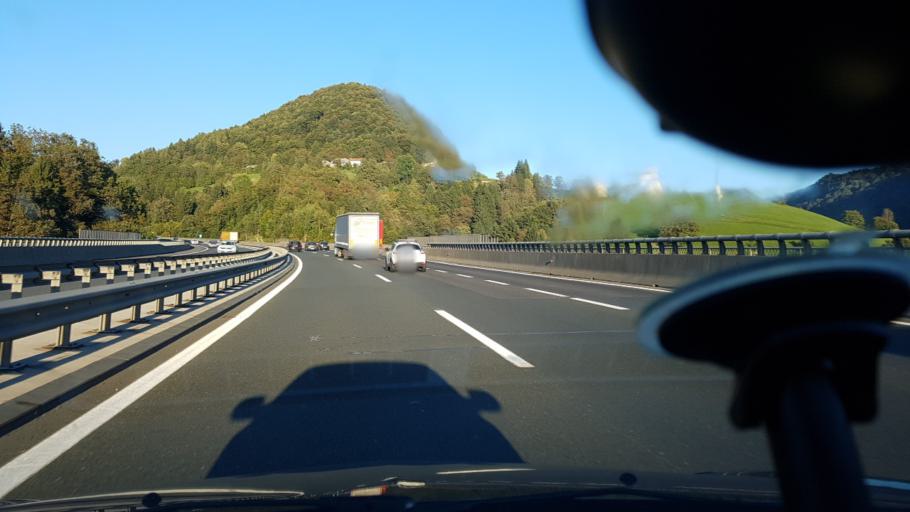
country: SI
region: Moravce
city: Moravce
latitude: 46.1762
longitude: 14.8256
